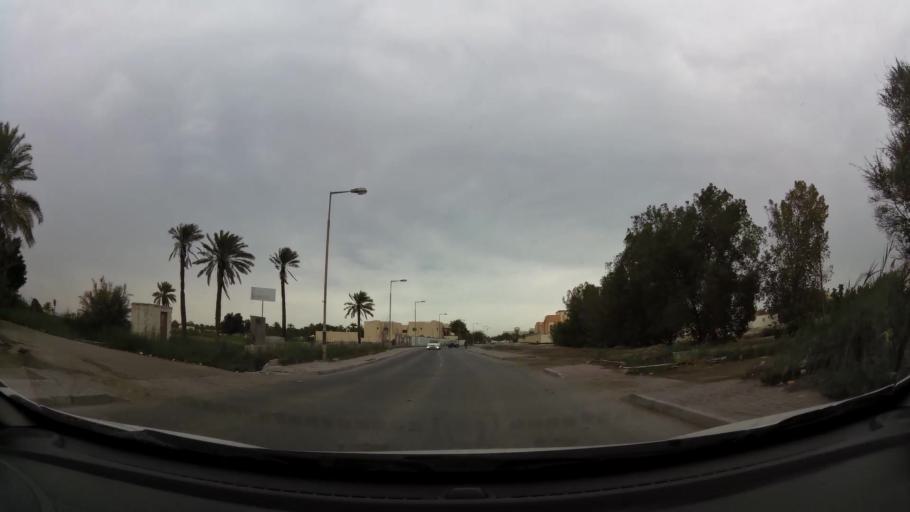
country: BH
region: Central Governorate
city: Madinat Hamad
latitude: 26.1458
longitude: 50.4568
